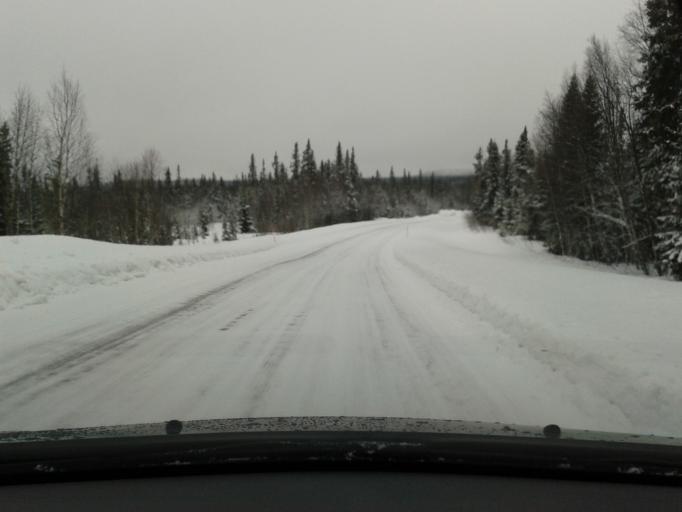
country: SE
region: Vaesterbotten
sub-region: Vilhelmina Kommun
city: Sjoberg
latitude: 65.1347
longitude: 15.8774
